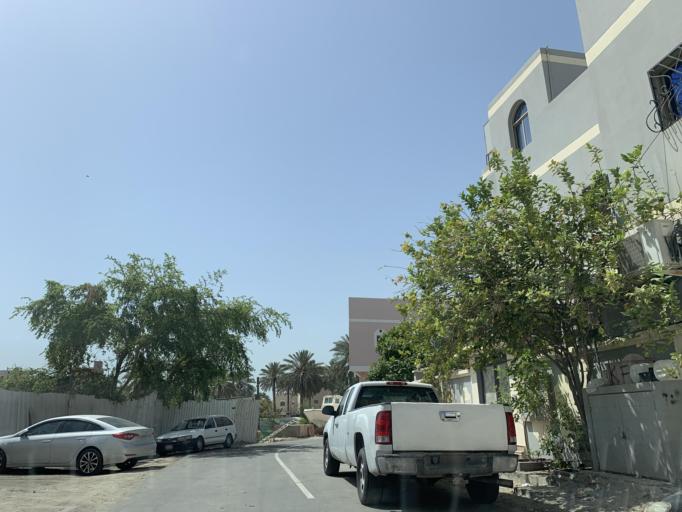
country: BH
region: Northern
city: Sitrah
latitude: 26.1450
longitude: 50.6054
